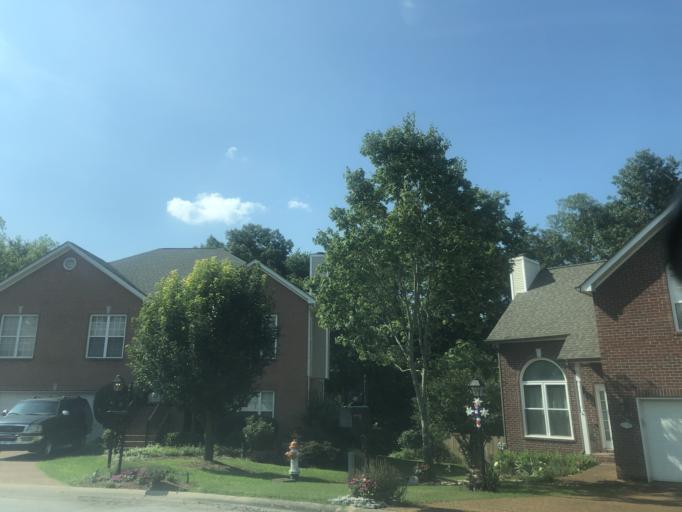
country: US
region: Tennessee
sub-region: Wilson County
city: Green Hill
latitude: 36.1516
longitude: -86.5879
